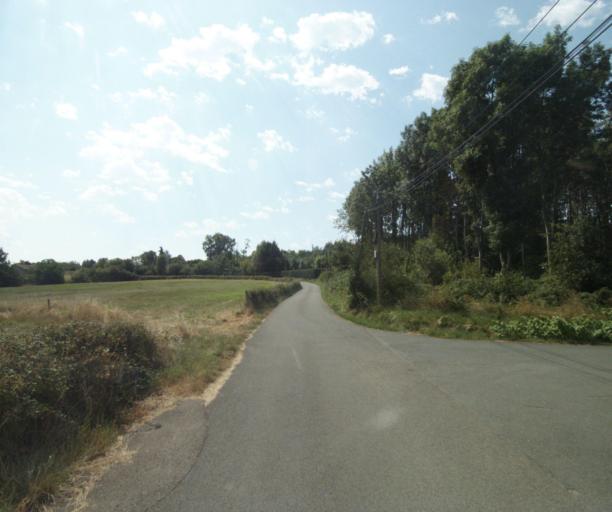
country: FR
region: Rhone-Alpes
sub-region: Departement du Rhone
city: Lentilly
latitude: 45.8495
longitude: 4.6532
